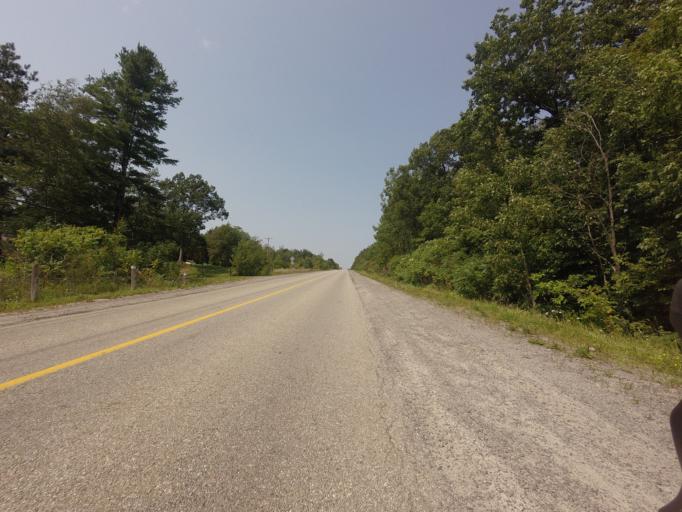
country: CA
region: Ontario
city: Perth
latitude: 44.6391
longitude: -76.5274
